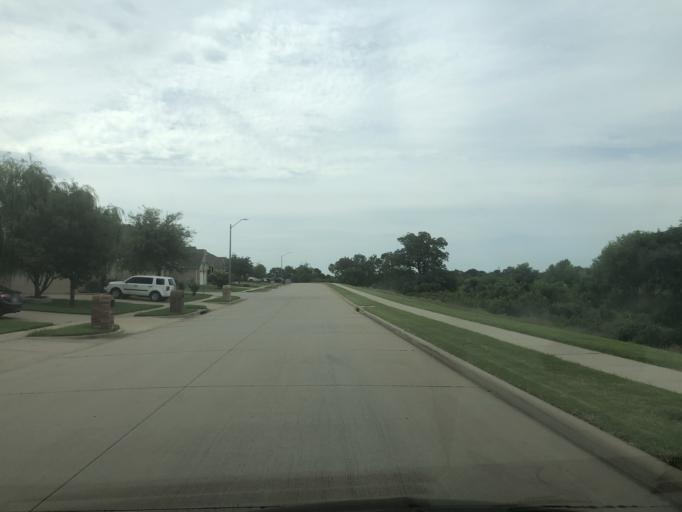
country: US
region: Texas
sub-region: Dallas County
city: Irving
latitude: 32.7960
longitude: -96.9897
